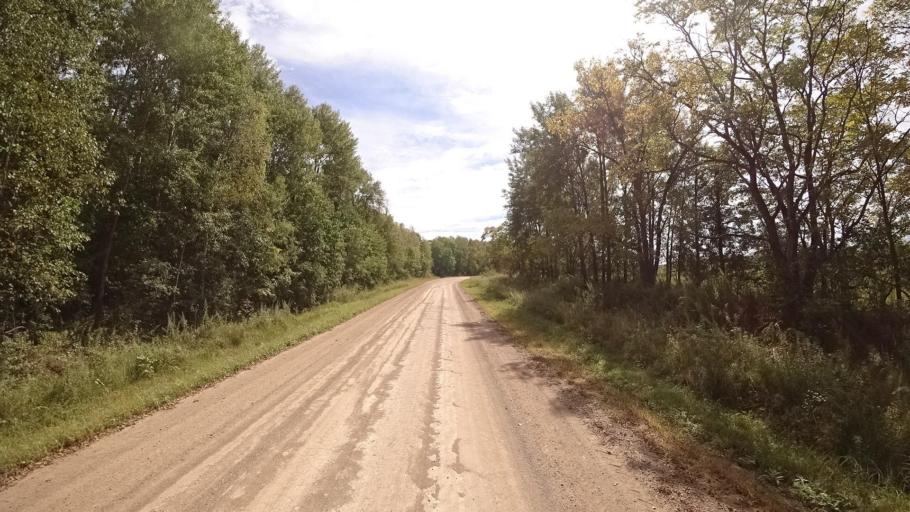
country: RU
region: Primorskiy
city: Yakovlevka
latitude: 44.6307
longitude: 133.6013
